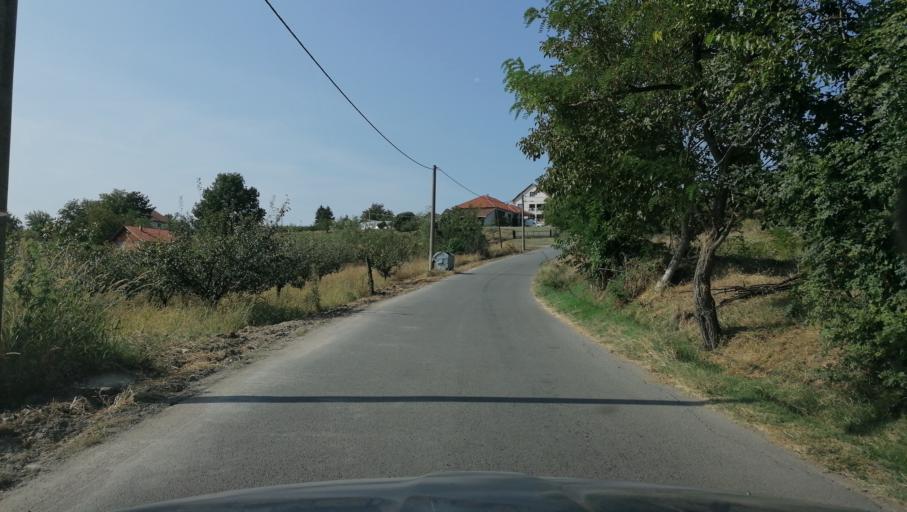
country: RS
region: Central Serbia
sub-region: Belgrade
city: Sopot
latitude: 44.5926
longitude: 20.6092
